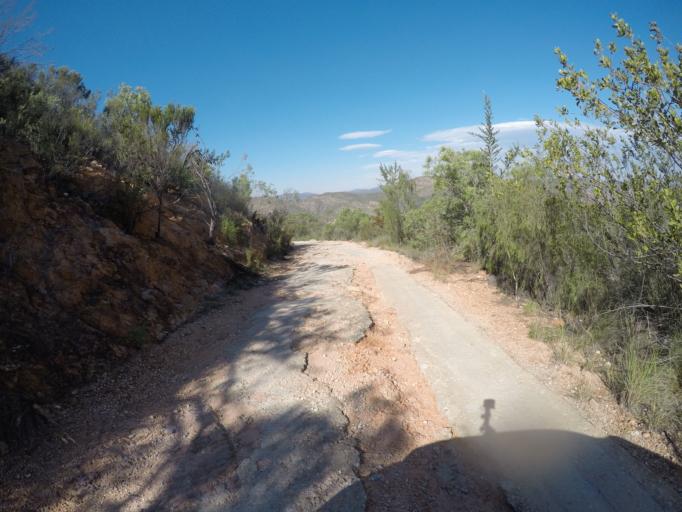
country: ZA
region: Eastern Cape
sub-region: Cacadu District Municipality
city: Kareedouw
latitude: -33.6395
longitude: 24.4535
